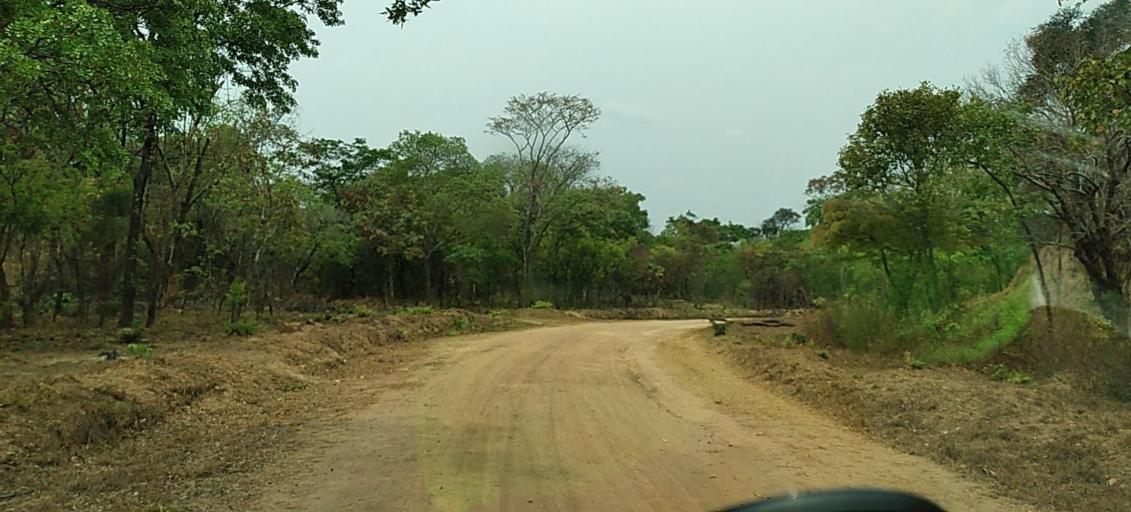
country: ZM
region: North-Western
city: Solwezi
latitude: -12.7829
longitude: 26.5207
